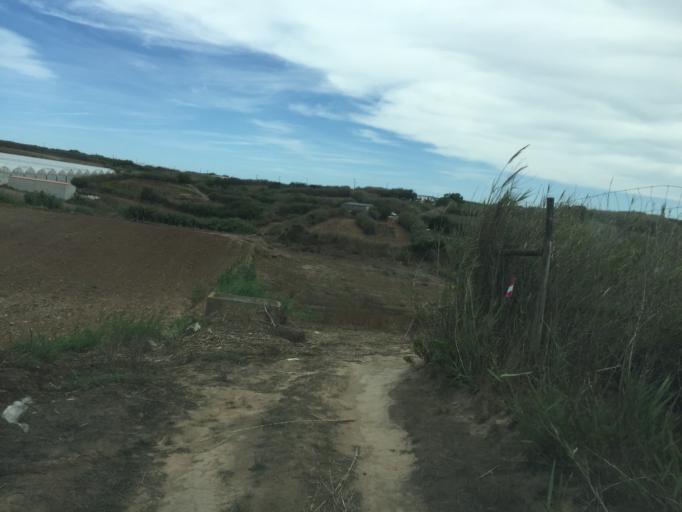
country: PT
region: Lisbon
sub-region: Lourinha
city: Lourinha
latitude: 39.1868
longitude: -9.3476
